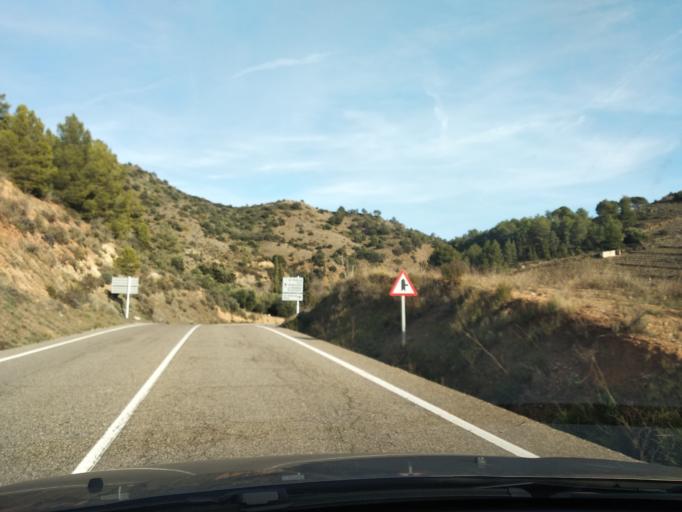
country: ES
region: Catalonia
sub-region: Provincia de Tarragona
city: Margalef
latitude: 41.2228
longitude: 0.7643
